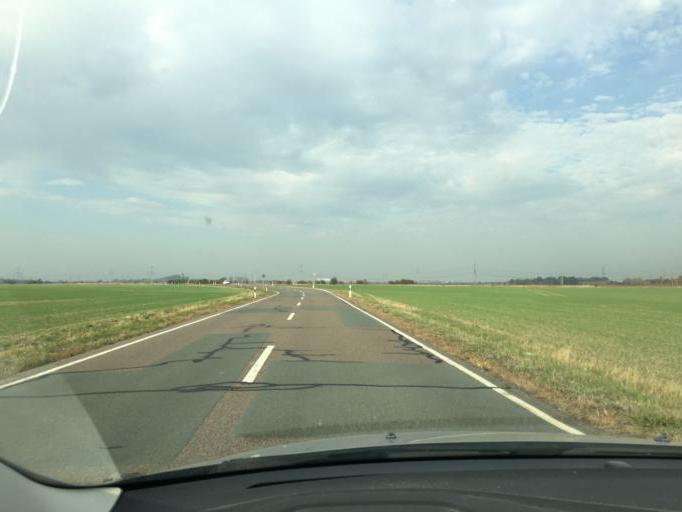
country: DE
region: Saxony
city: Wiedemar
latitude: 51.5014
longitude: 12.1977
